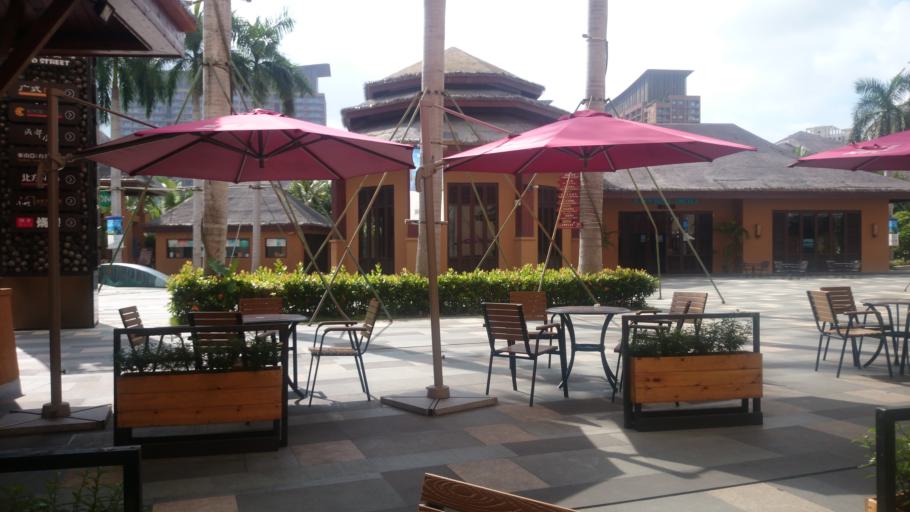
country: CN
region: Hainan
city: Fenghuang
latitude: 18.2874
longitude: 109.4871
